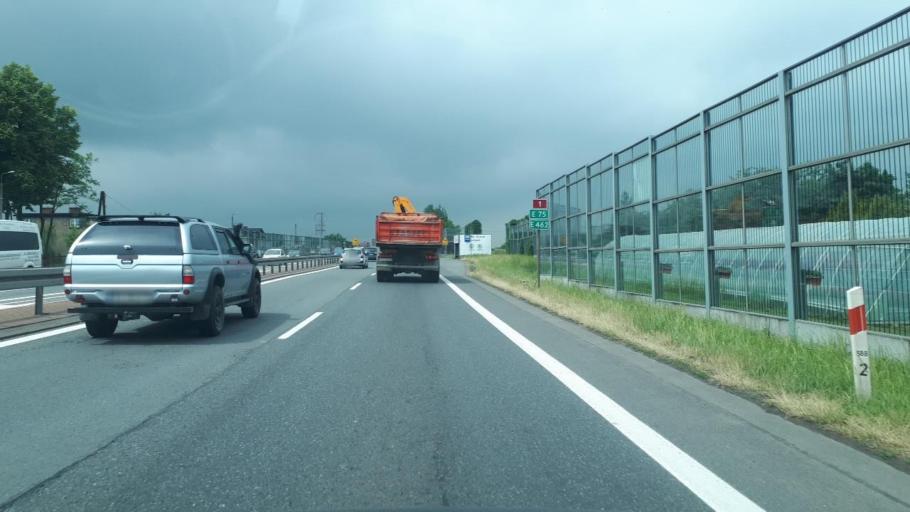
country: PL
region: Silesian Voivodeship
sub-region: Powiat pszczynski
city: Goczalkowice Zdroj
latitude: 49.9474
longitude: 18.9722
